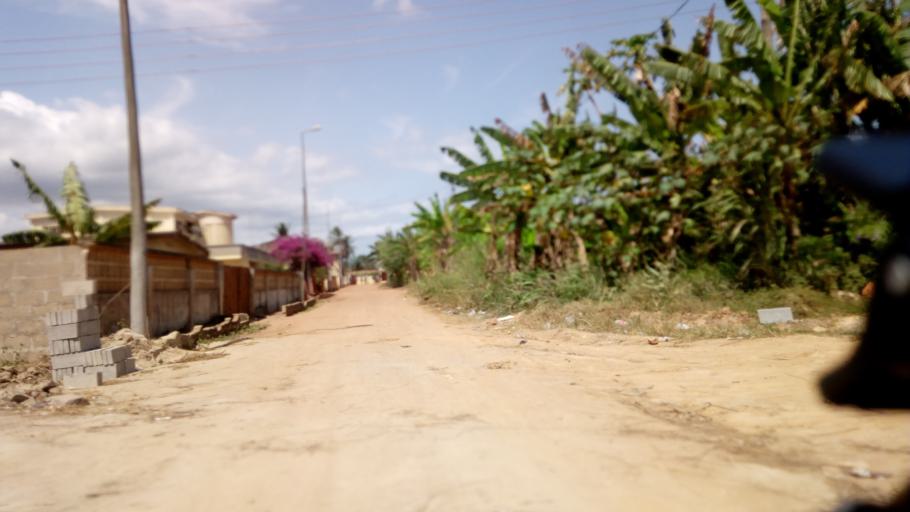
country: GH
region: Central
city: Cape Coast
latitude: 5.1325
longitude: -1.2804
